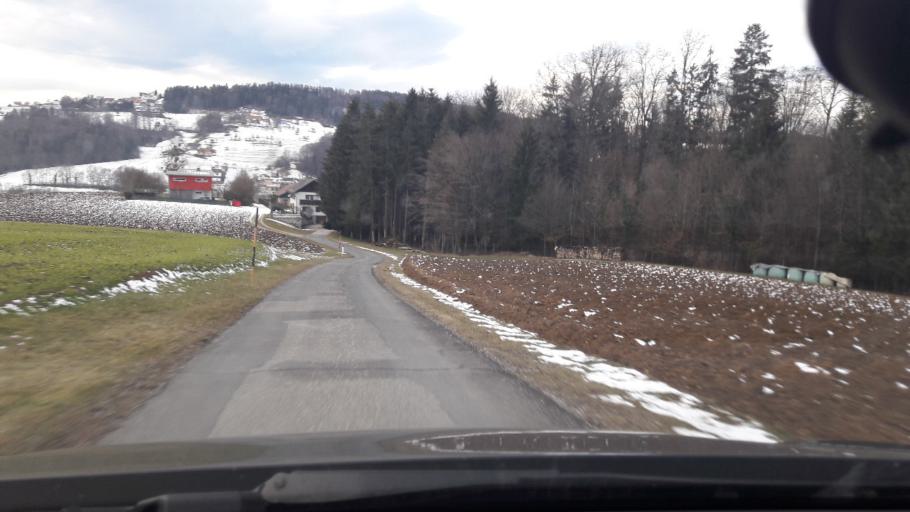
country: AT
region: Styria
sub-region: Politischer Bezirk Graz-Umgebung
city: Sankt Oswald bei Plankenwarth
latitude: 47.0741
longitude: 15.2729
